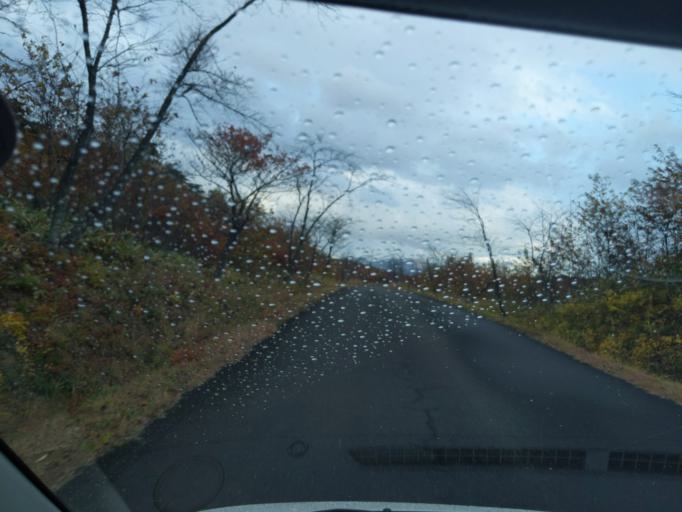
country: JP
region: Iwate
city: Mizusawa
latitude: 39.0854
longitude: 141.0134
